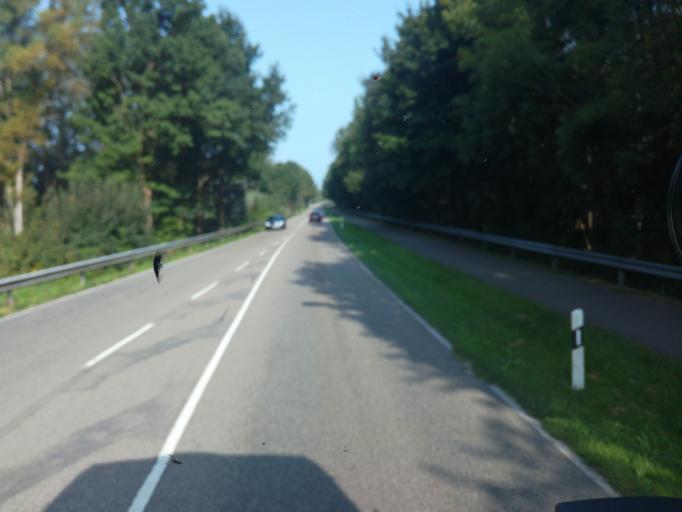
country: DE
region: Baden-Wuerttemberg
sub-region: Karlsruhe Region
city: Rastatt
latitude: 48.8472
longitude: 8.1996
